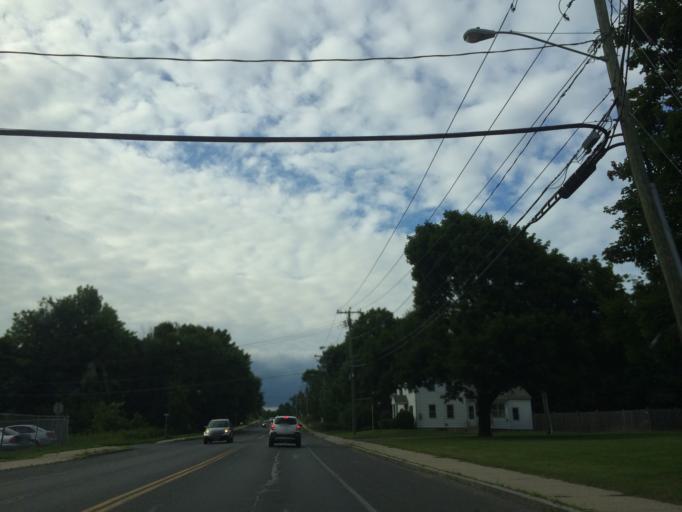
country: US
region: Massachusetts
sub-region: Berkshire County
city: Pittsfield
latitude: 42.4776
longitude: -73.2451
